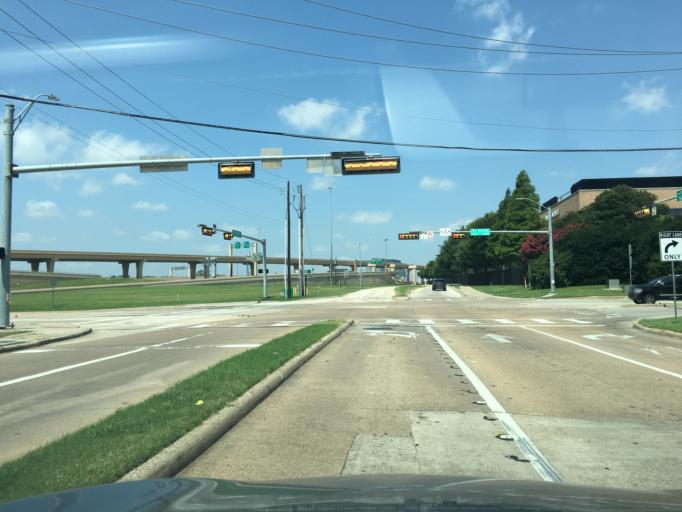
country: US
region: Texas
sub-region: Dallas County
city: Richardson
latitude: 32.9231
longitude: -96.7491
